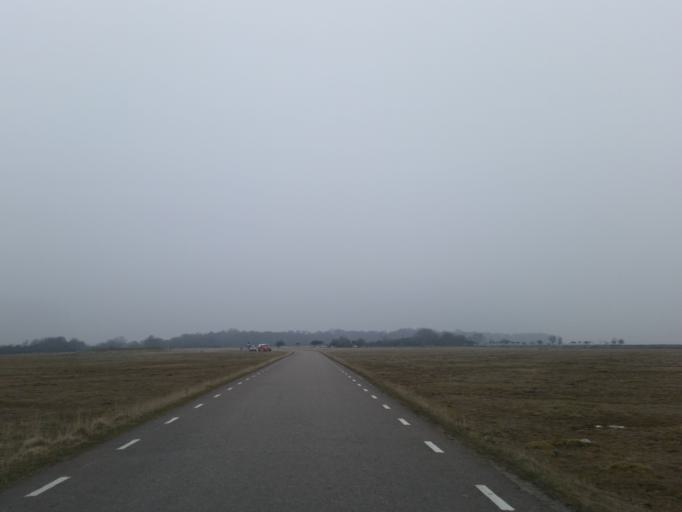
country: SE
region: Kalmar
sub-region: Morbylanga Kommun
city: Moerbylanga
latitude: 56.2077
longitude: 16.4048
